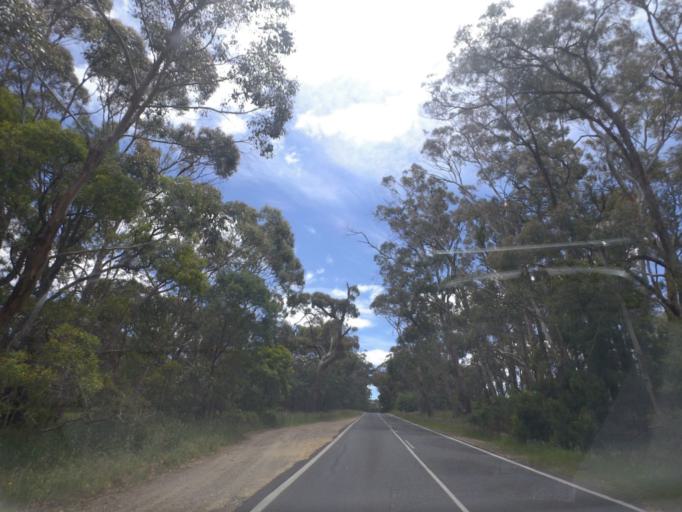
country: AU
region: Victoria
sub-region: Mount Alexander
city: Castlemaine
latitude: -37.3281
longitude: 144.1653
